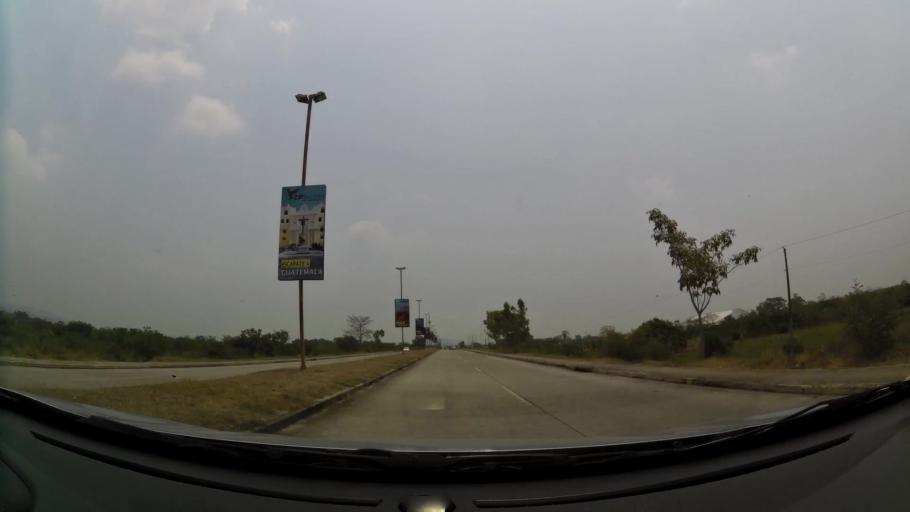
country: HN
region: Cortes
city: La Lima
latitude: 15.4545
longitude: -87.9325
